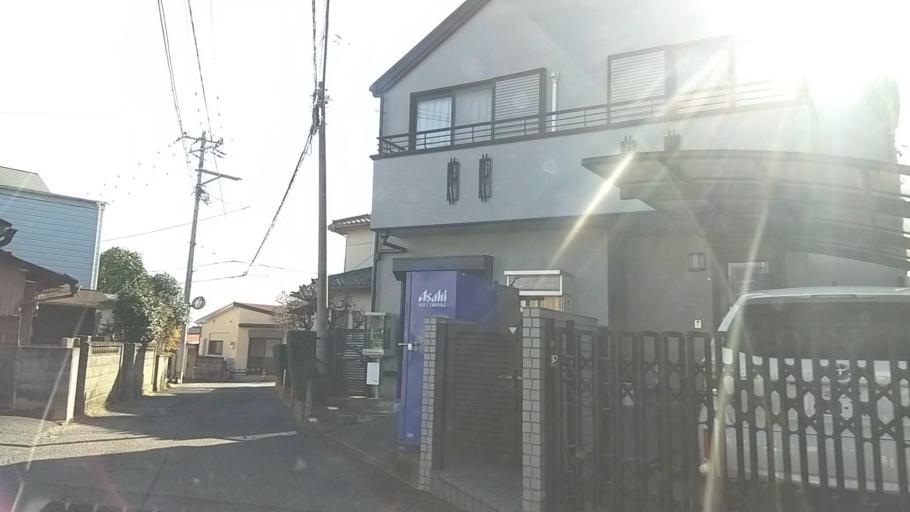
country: JP
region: Kanagawa
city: Hadano
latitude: 35.3735
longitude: 139.2298
